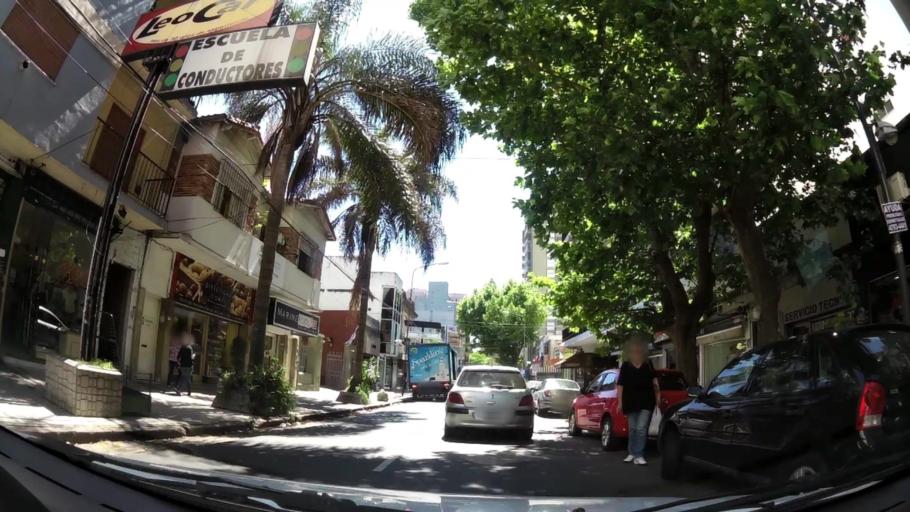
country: AR
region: Buenos Aires
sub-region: Partido de Vicente Lopez
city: Olivos
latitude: -34.5136
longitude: -58.4904
